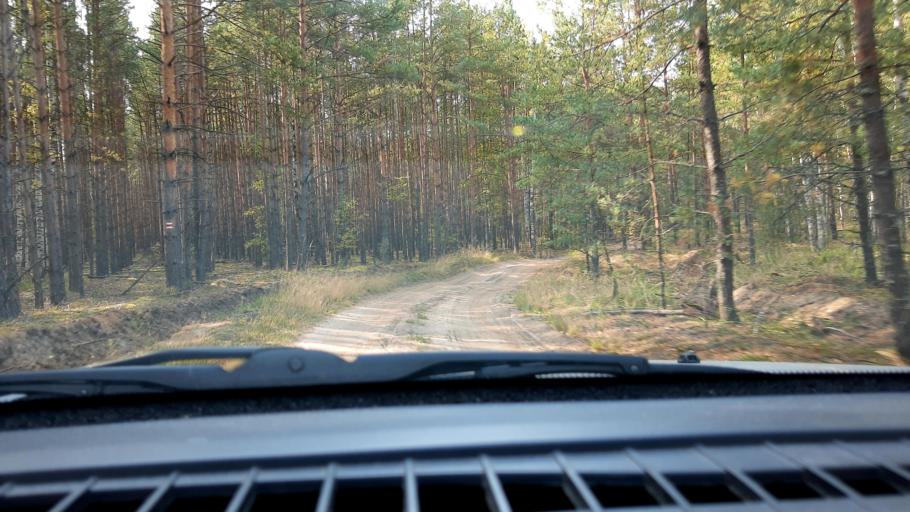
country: RU
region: Nizjnij Novgorod
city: Gidrotorf
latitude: 56.3802
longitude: 43.5384
